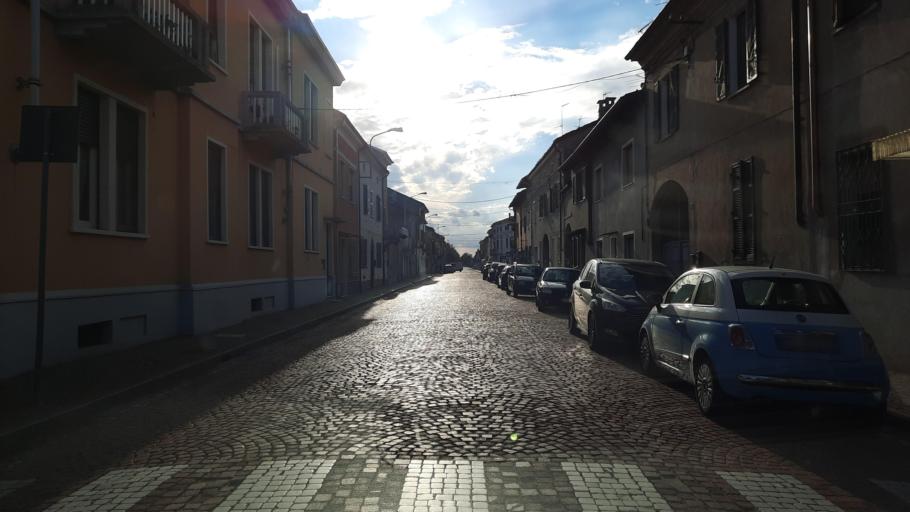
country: IT
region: Piedmont
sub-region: Provincia di Vercelli
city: Fontanetto Po
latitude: 45.1947
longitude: 8.1942
